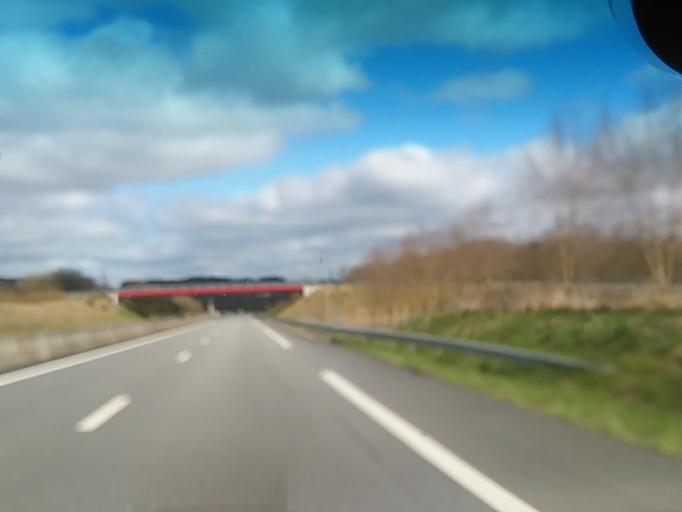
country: FR
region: Haute-Normandie
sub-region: Departement de l'Eure
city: Bourg-Achard
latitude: 49.2776
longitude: 0.7732
